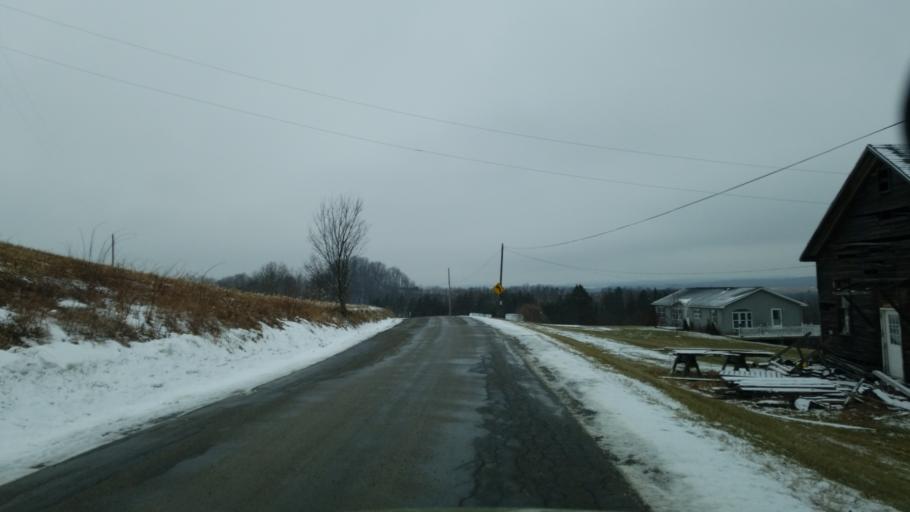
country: US
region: Pennsylvania
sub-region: Jefferson County
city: Sykesville
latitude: 41.0847
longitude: -78.8320
